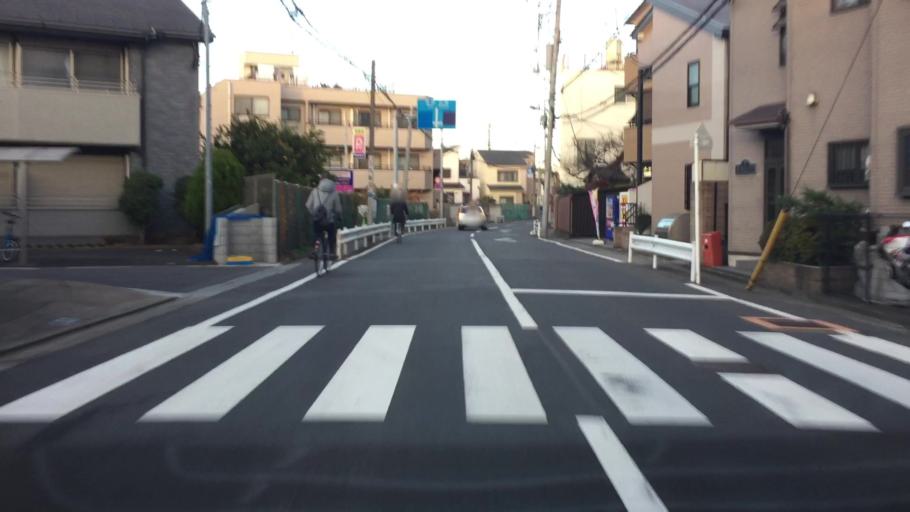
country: JP
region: Saitama
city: Soka
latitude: 35.7700
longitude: 139.8095
